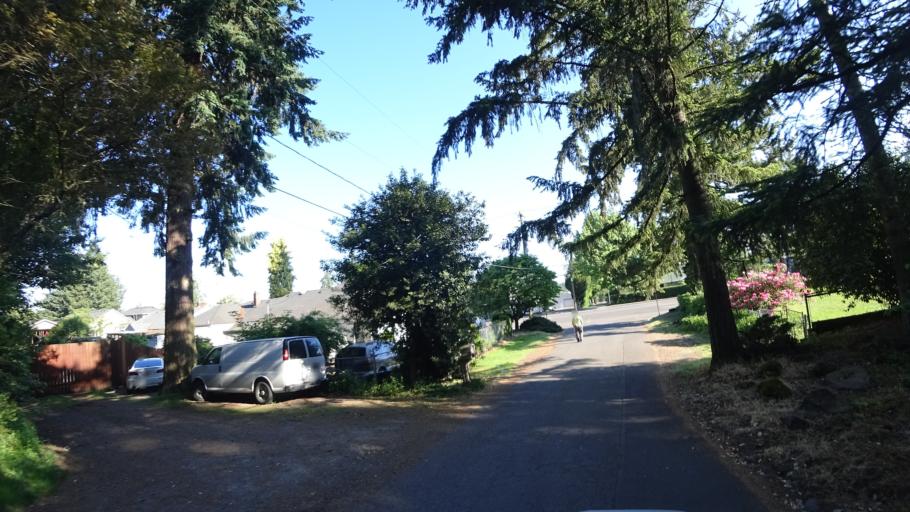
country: US
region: Oregon
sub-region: Multnomah County
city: Lents
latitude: 45.4760
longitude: -122.5413
